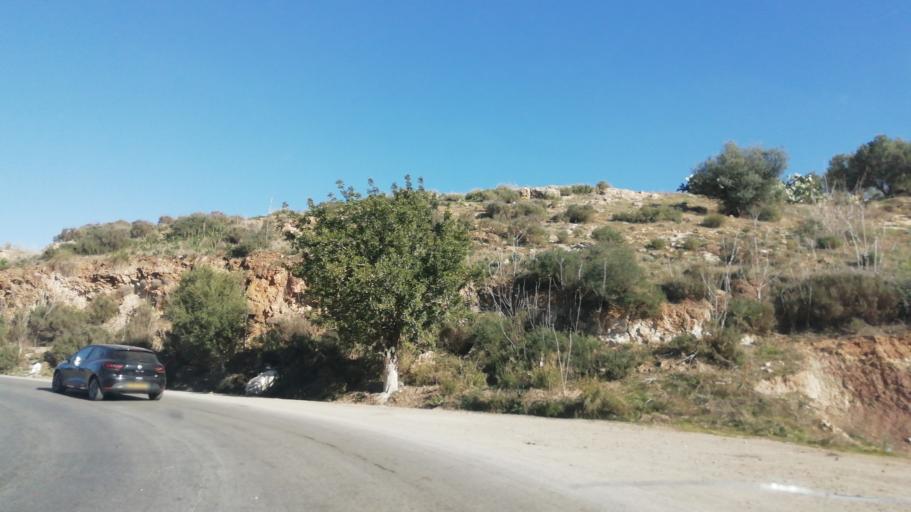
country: DZ
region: Tlemcen
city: Beni Mester
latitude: 34.8293
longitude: -1.5066
